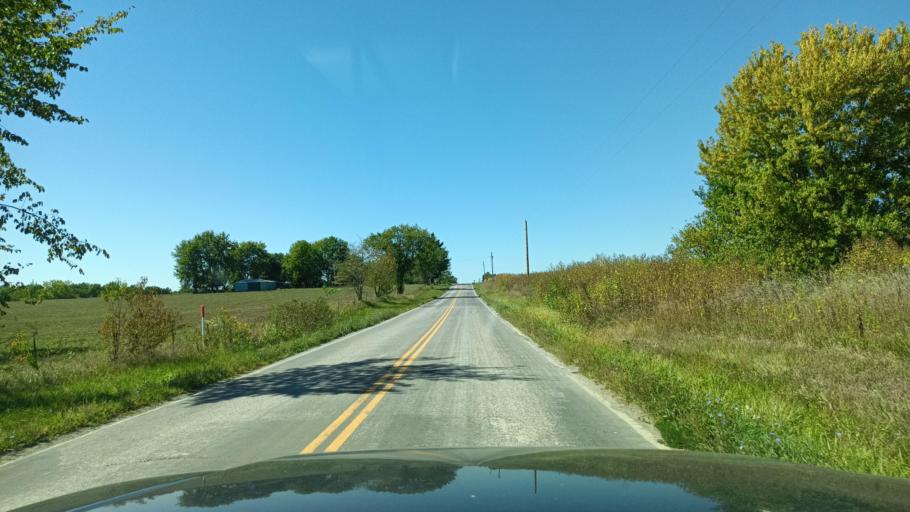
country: US
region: Missouri
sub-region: Macon County
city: La Plata
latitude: 40.0224
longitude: -92.5621
